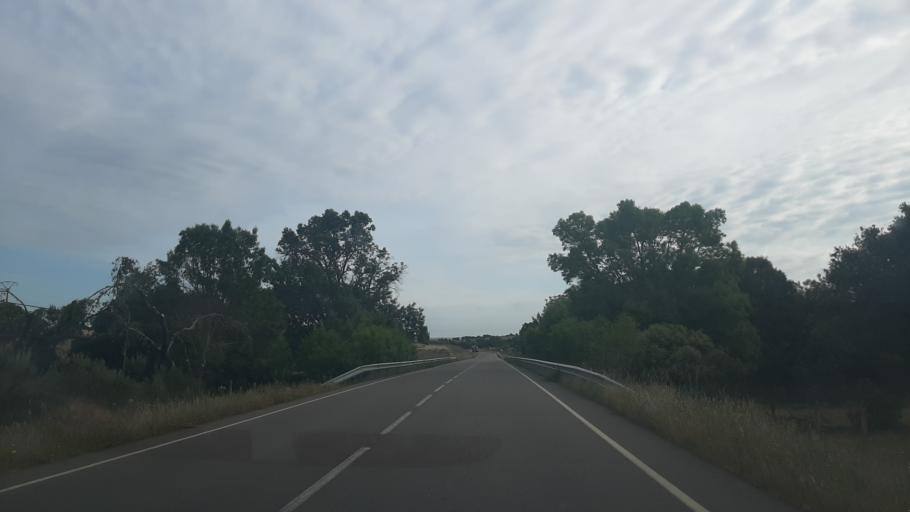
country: ES
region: Castille and Leon
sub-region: Provincia de Salamanca
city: Espeja
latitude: 40.5965
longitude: -6.7041
